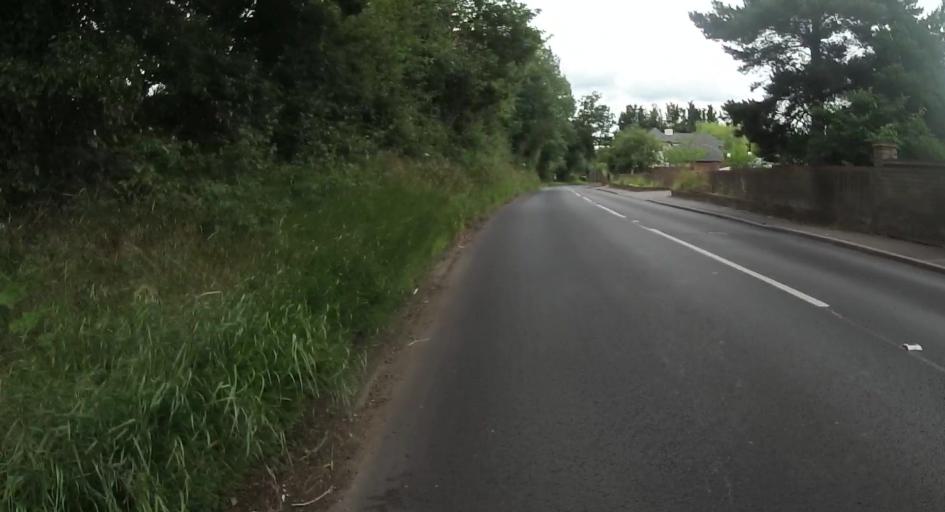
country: GB
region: England
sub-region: Wokingham
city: Barkham
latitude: 51.3955
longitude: -0.8799
